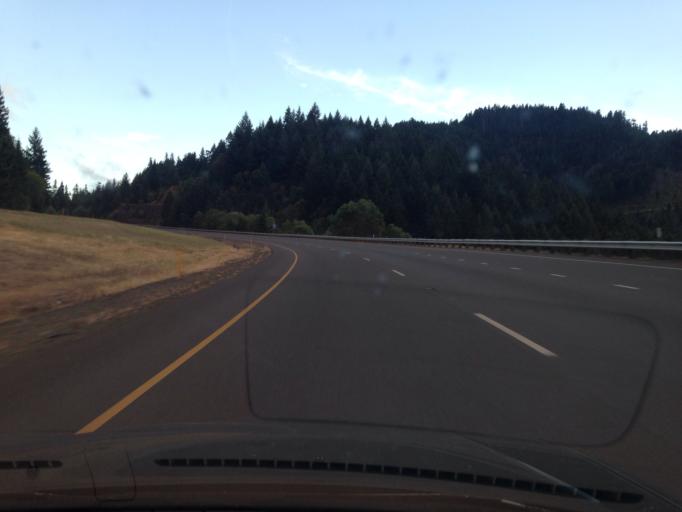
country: US
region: Oregon
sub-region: Douglas County
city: Canyonville
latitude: 42.7438
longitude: -123.3729
